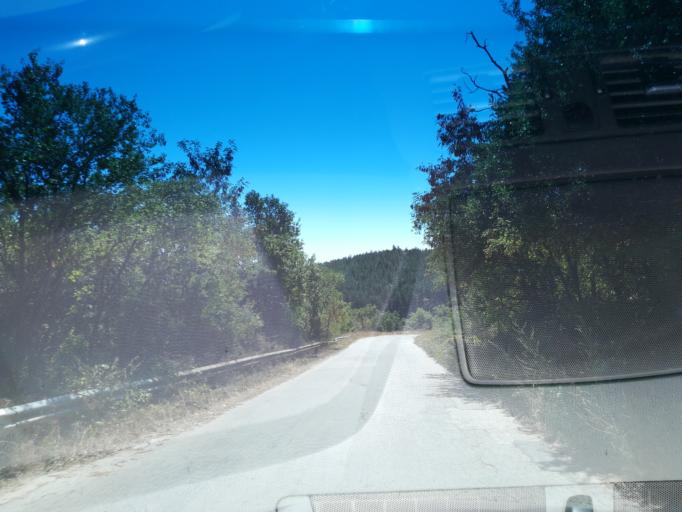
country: BG
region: Pazardzhik
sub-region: Obshtina Strelcha
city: Strelcha
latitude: 42.5279
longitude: 24.3294
